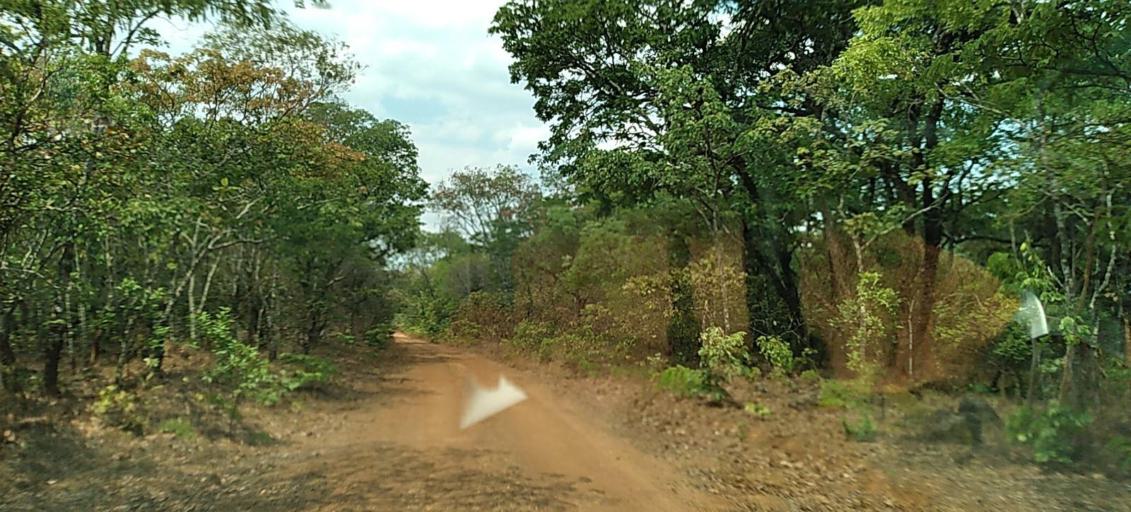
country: ZM
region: Copperbelt
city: Chililabombwe
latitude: -12.4545
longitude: 27.6067
